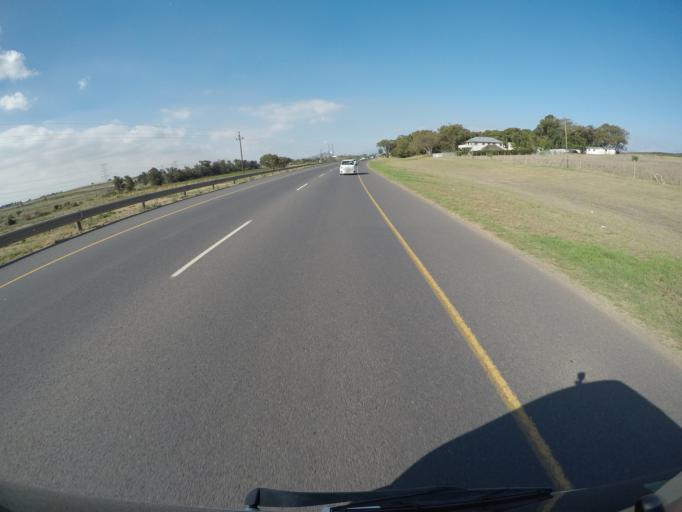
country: ZA
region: Western Cape
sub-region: City of Cape Town
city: Kraaifontein
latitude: -33.8844
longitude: 18.7509
